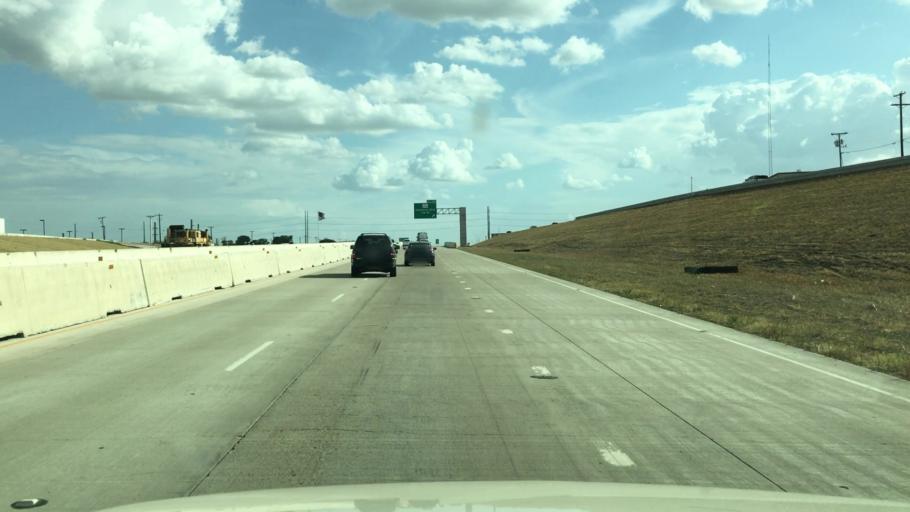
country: US
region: Texas
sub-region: Bell County
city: Temple
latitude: 31.1381
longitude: -97.3305
